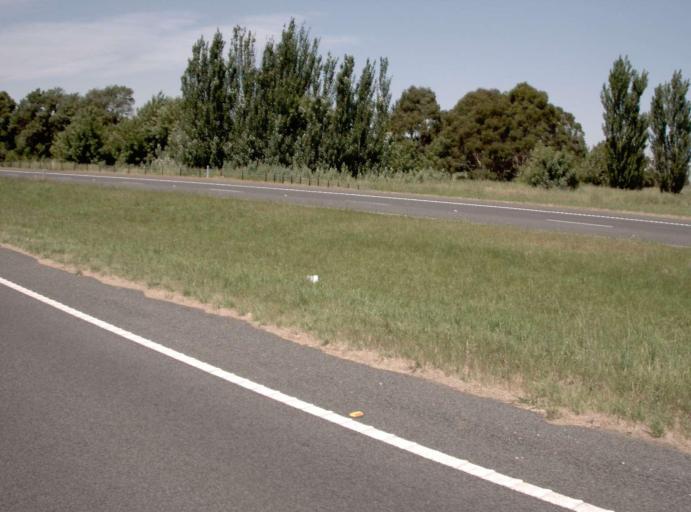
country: AU
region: Victoria
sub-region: Latrobe
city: Morwell
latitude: -38.2447
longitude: 146.4378
